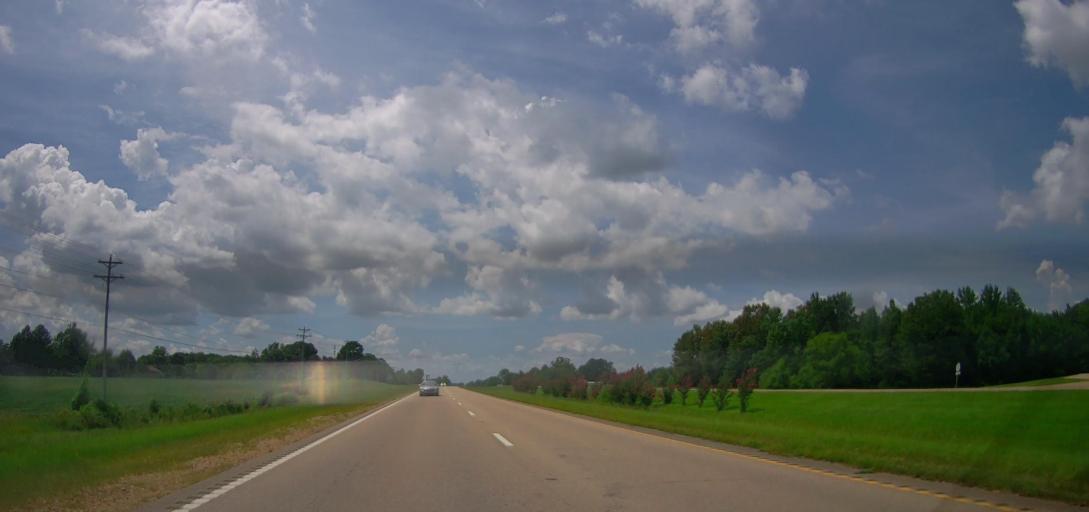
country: US
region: Mississippi
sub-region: Lee County
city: Shannon
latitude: 34.1107
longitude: -88.6855
